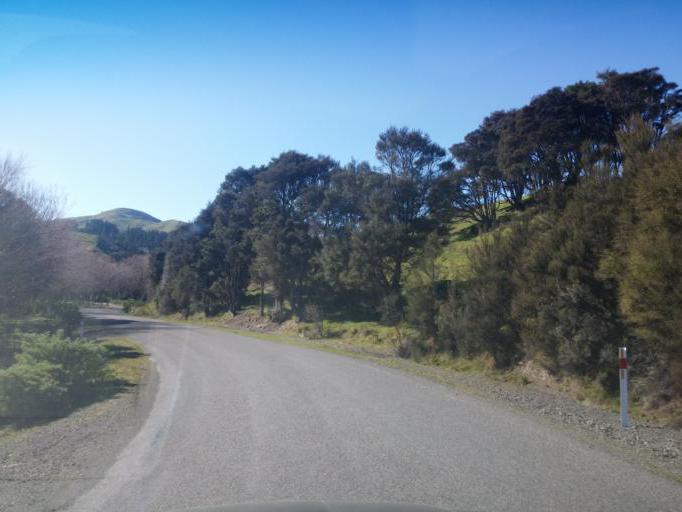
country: NZ
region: Wellington
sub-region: South Wairarapa District
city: Waipawa
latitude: -41.4182
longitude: 175.4909
